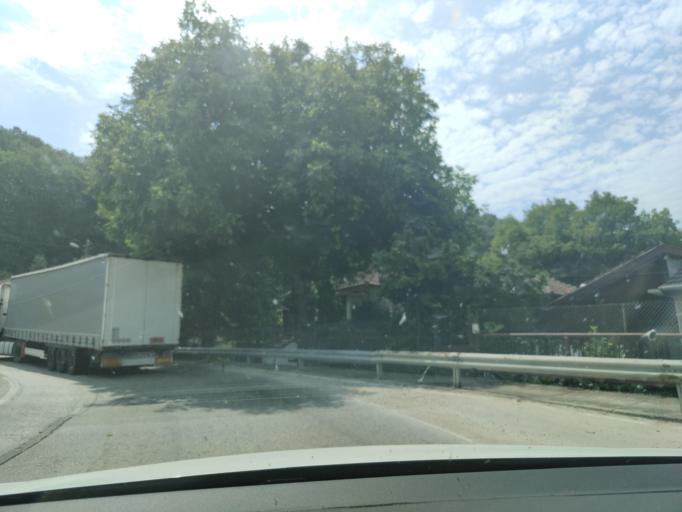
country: BG
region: Vidin
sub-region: Obshtina Dimovo
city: Dimovo
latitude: 43.7352
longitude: 22.7218
